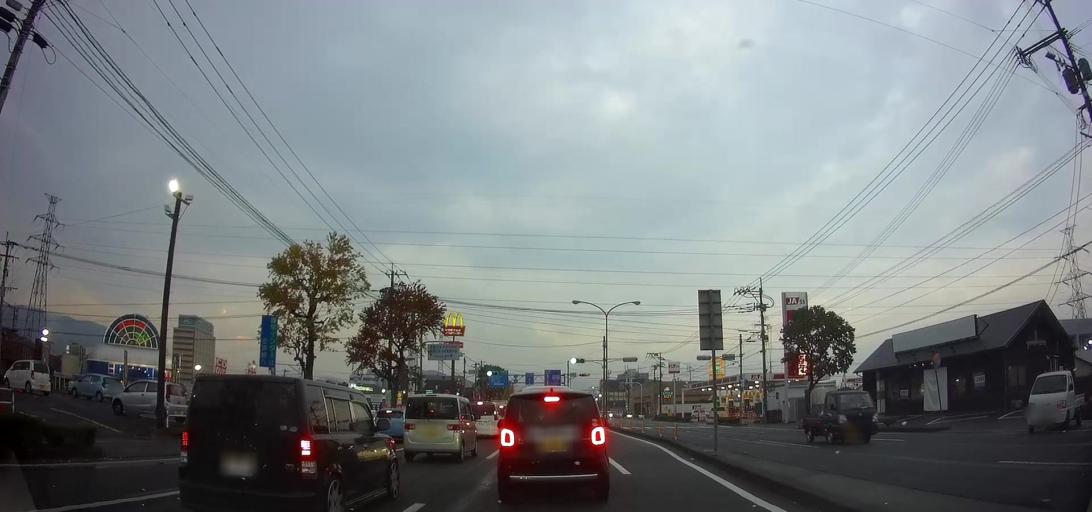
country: JP
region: Nagasaki
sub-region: Isahaya-shi
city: Isahaya
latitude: 32.8374
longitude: 130.0163
